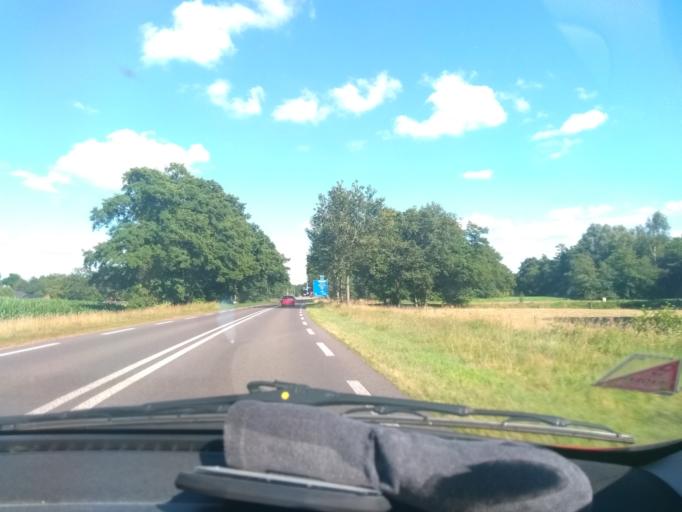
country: NL
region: Drenthe
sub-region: Gemeente Tynaarlo
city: Vries
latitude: 53.0817
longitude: 6.5772
